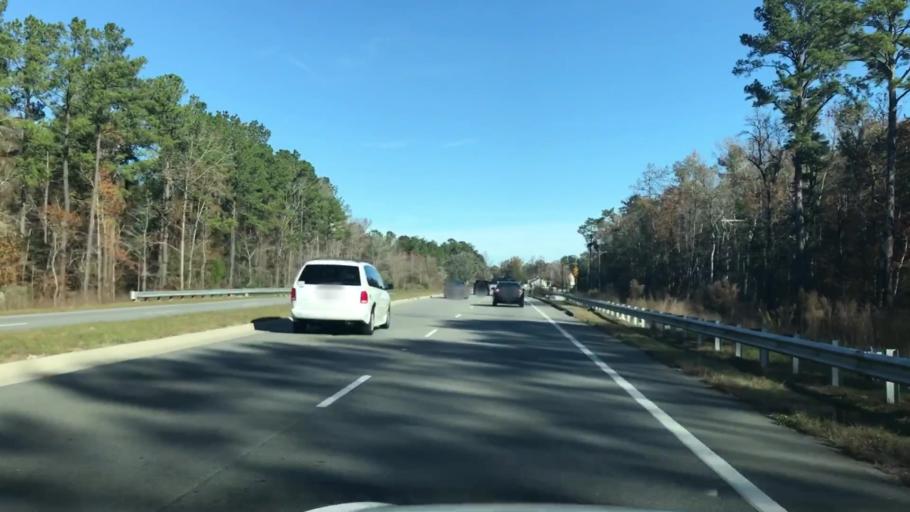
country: US
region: South Carolina
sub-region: Dorchester County
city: Centerville
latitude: 32.9544
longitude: -80.2016
